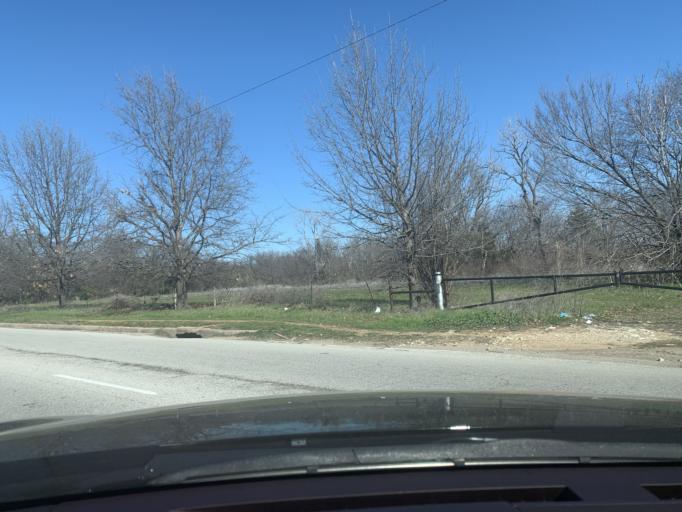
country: US
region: Texas
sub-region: Tarrant County
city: Haltom City
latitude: 32.7622
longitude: -97.2877
